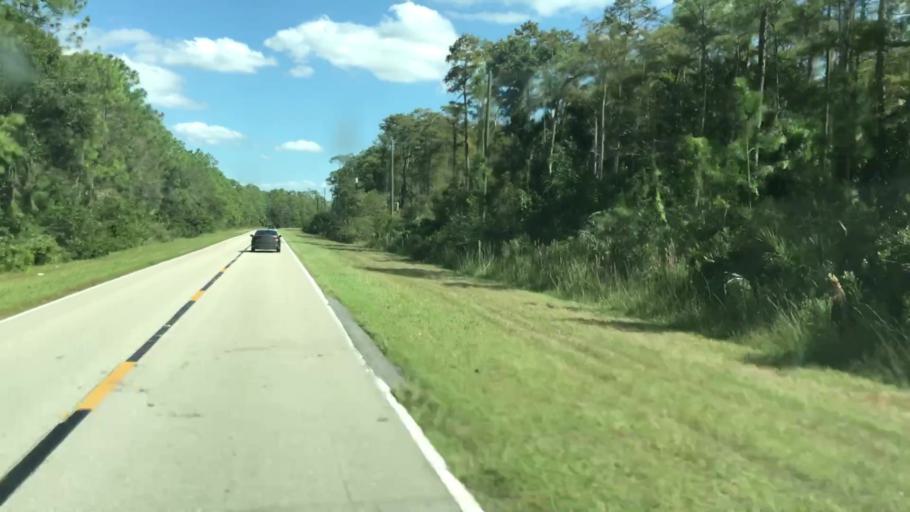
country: US
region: Florida
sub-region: Lee County
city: Alva
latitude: 26.6775
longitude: -81.6087
